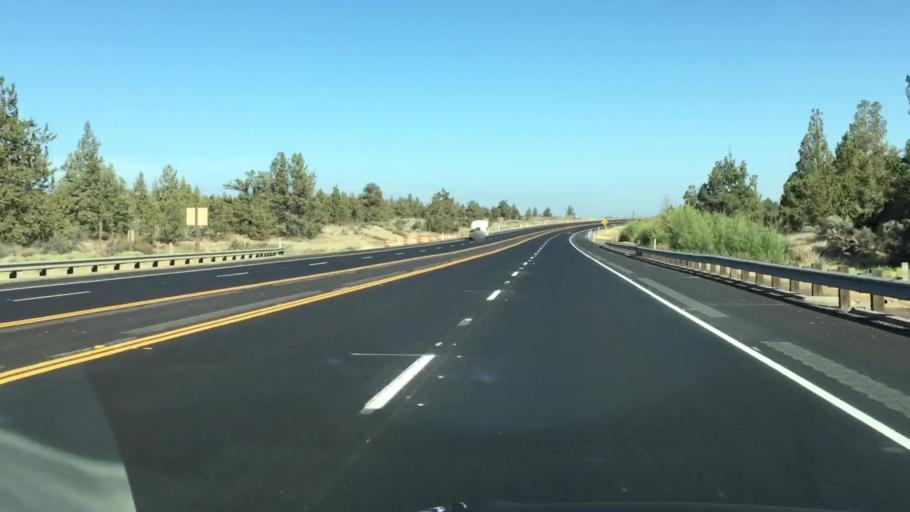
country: US
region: Oregon
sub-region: Deschutes County
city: Terrebonne
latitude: 44.3943
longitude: -121.1944
